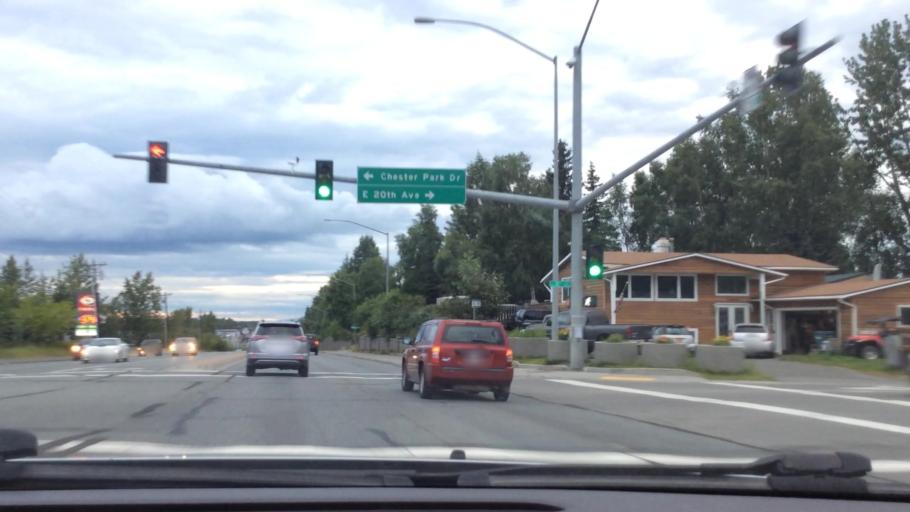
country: US
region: Alaska
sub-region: Anchorage Municipality
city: Elmendorf Air Force Base
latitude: 61.2025
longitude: -149.7334
